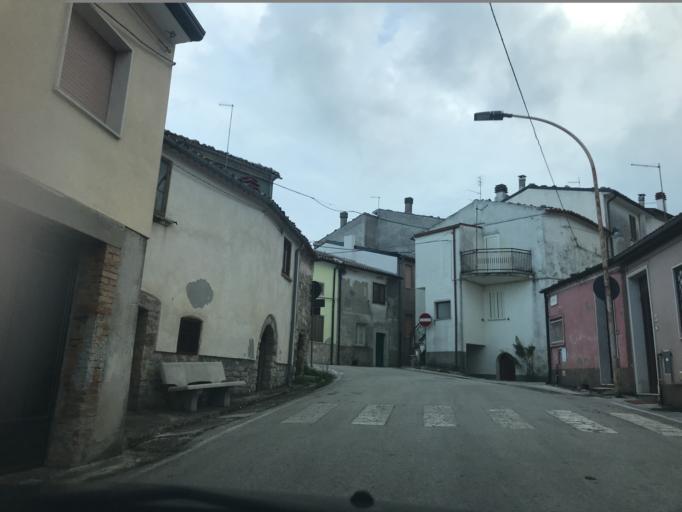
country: IT
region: Molise
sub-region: Provincia di Campobasso
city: Duronia
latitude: 41.6597
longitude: 14.4592
